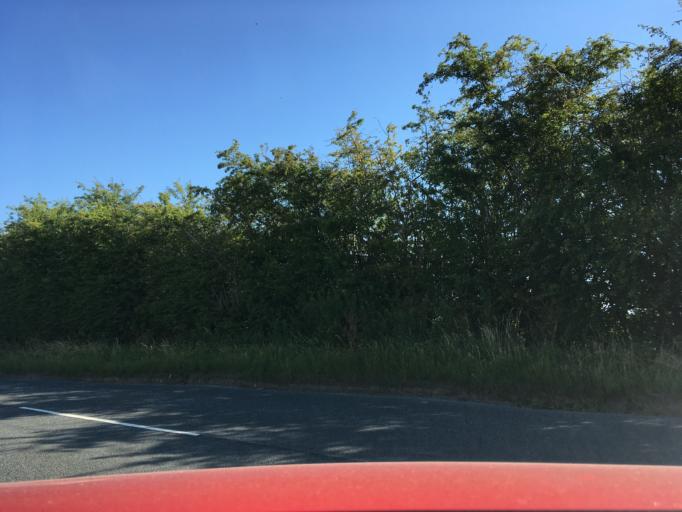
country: GB
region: England
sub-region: South Gloucestershire
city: Pucklechurch
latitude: 51.4849
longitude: -2.4300
